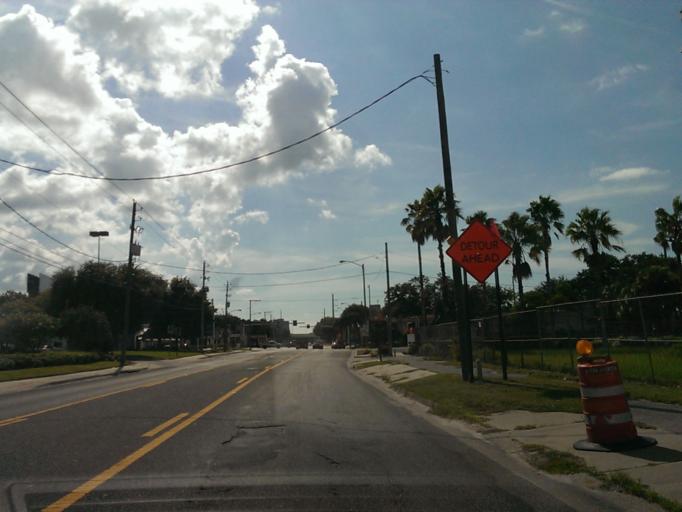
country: US
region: Florida
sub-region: Hillsborough County
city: Tampa
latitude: 27.9522
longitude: -82.5037
